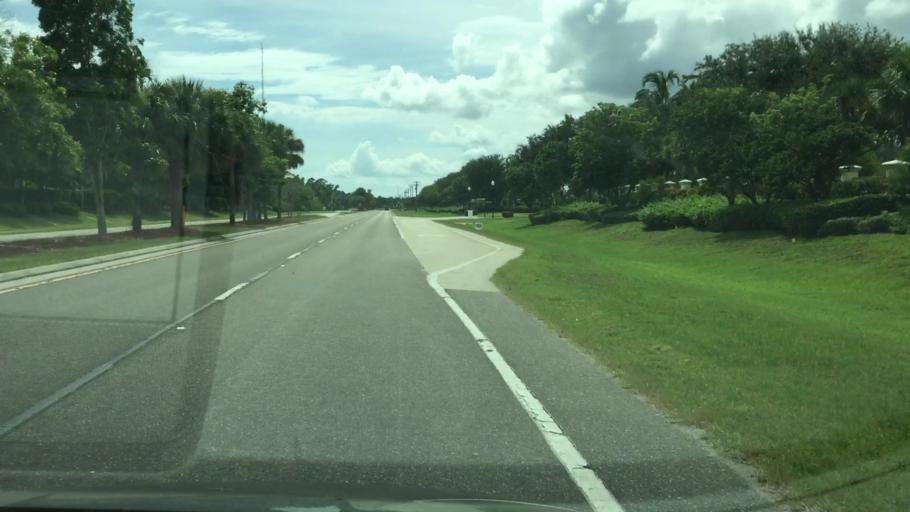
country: US
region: Florida
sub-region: Lee County
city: Estero
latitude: 26.4492
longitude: -81.8064
